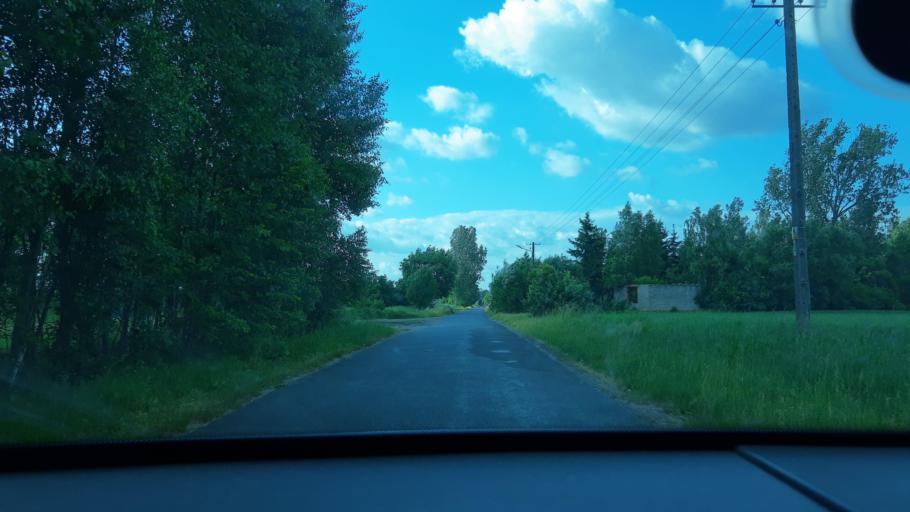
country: PL
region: Lodz Voivodeship
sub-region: Powiat zdunskowolski
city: Zapolice
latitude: 51.5198
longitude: 18.8441
